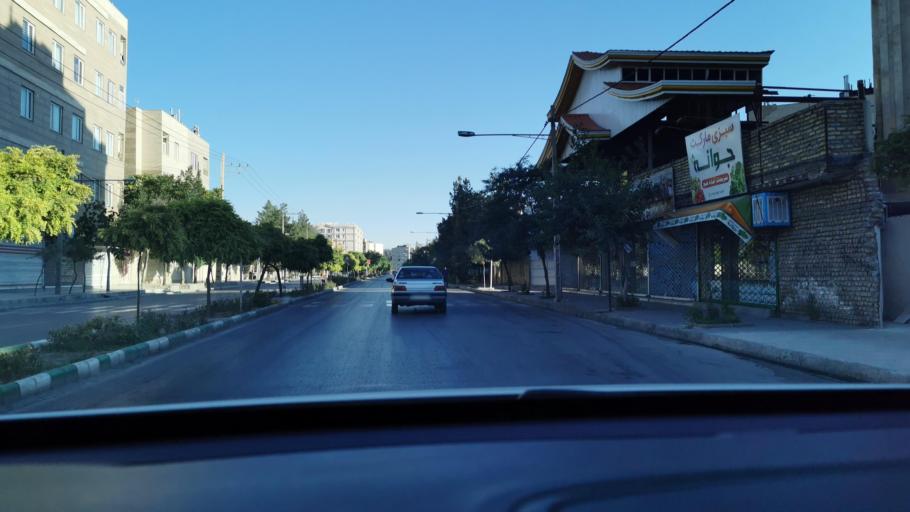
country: IR
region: Razavi Khorasan
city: Mashhad
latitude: 36.3573
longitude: 59.4866
